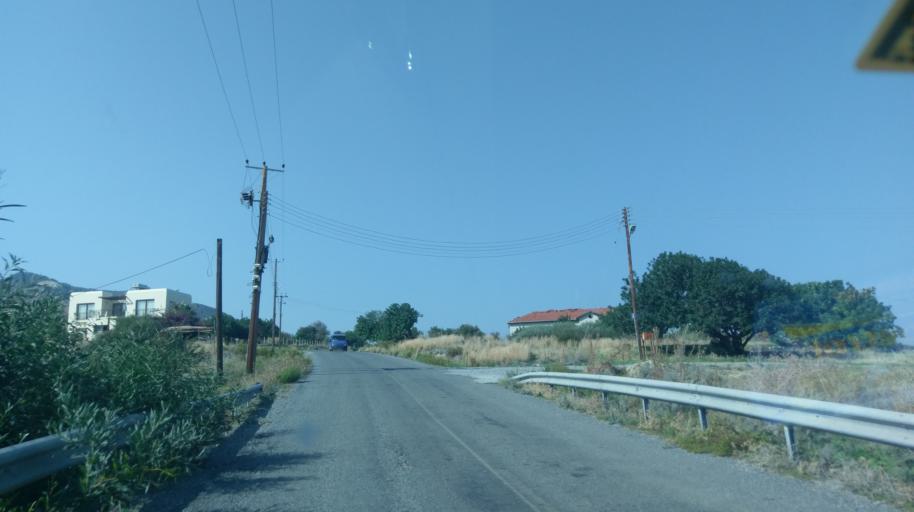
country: CY
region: Keryneia
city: Lapithos
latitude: 35.3619
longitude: 33.0357
